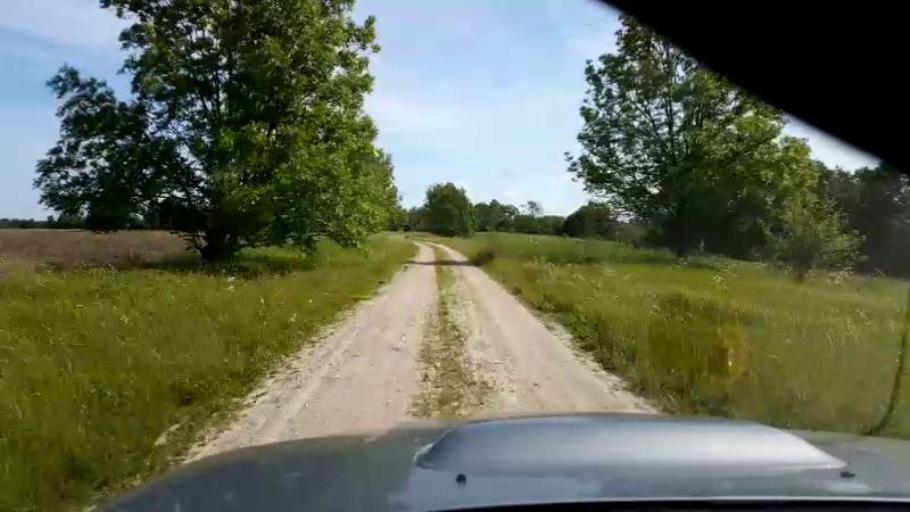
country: EE
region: Paernumaa
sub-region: Sauga vald
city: Sauga
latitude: 58.4949
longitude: 24.5367
